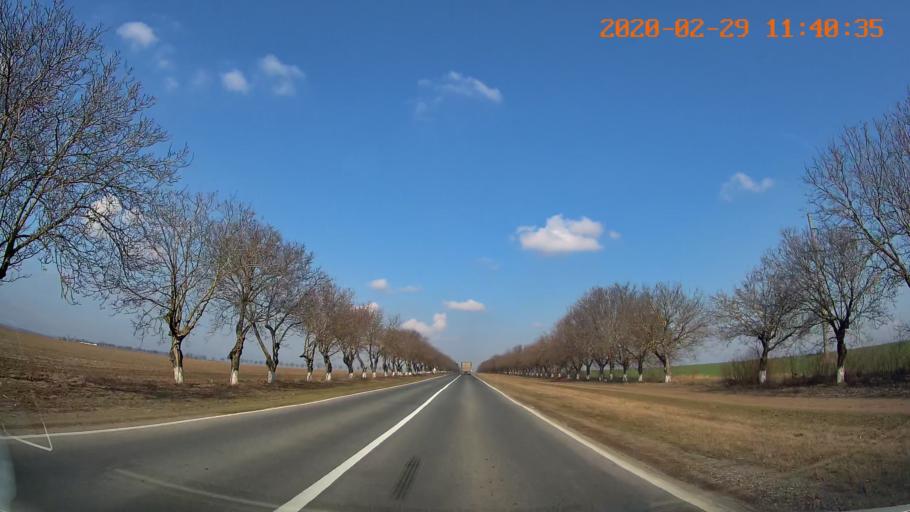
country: MD
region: Rezina
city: Saharna
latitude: 47.6587
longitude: 29.0196
